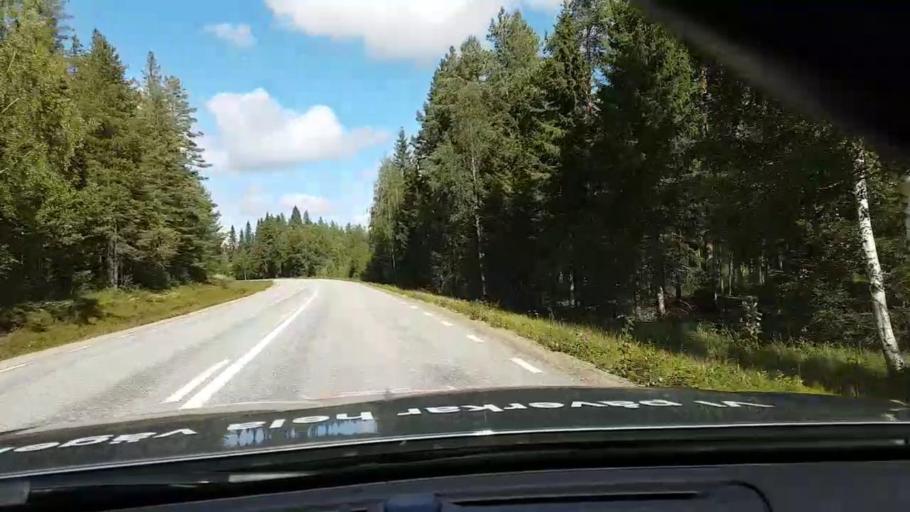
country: SE
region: Vaesternorrland
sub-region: OErnskoeldsviks Kommun
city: Bredbyn
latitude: 63.6281
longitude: 17.9101
